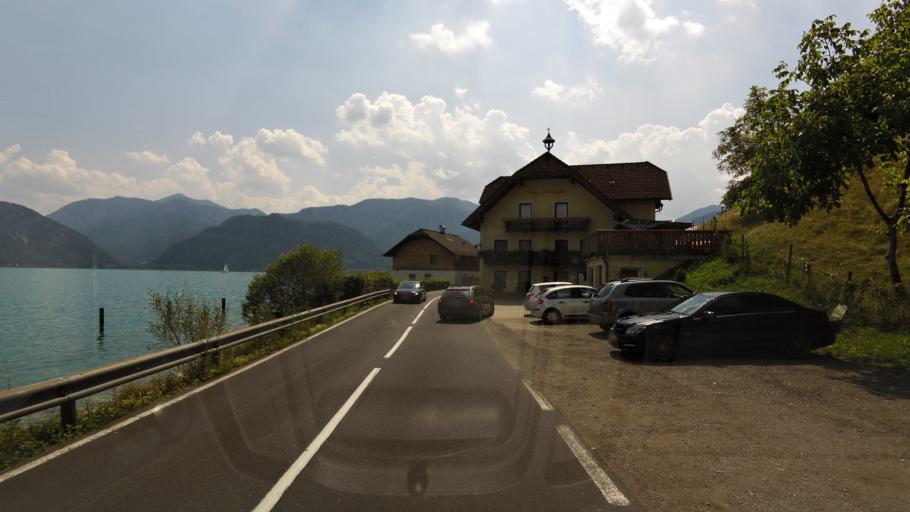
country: AT
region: Upper Austria
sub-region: Politischer Bezirk Vocklabruck
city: Steinbach am Attersee
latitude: 47.8226
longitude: 13.5104
